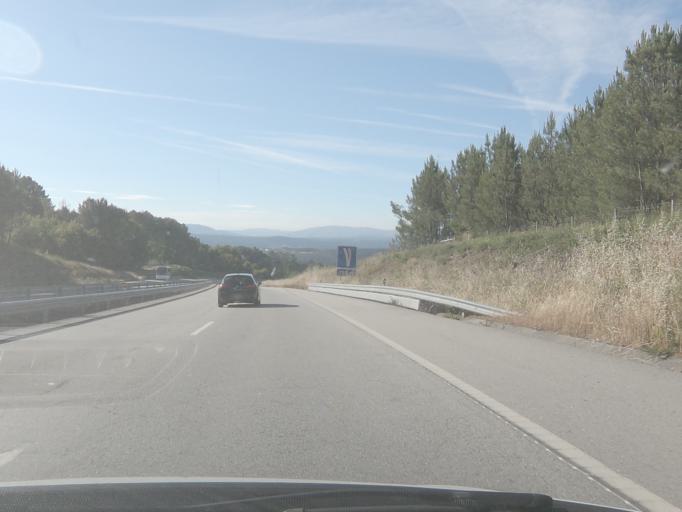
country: PT
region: Viseu
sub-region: Viseu
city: Campo
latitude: 40.7338
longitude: -7.9221
